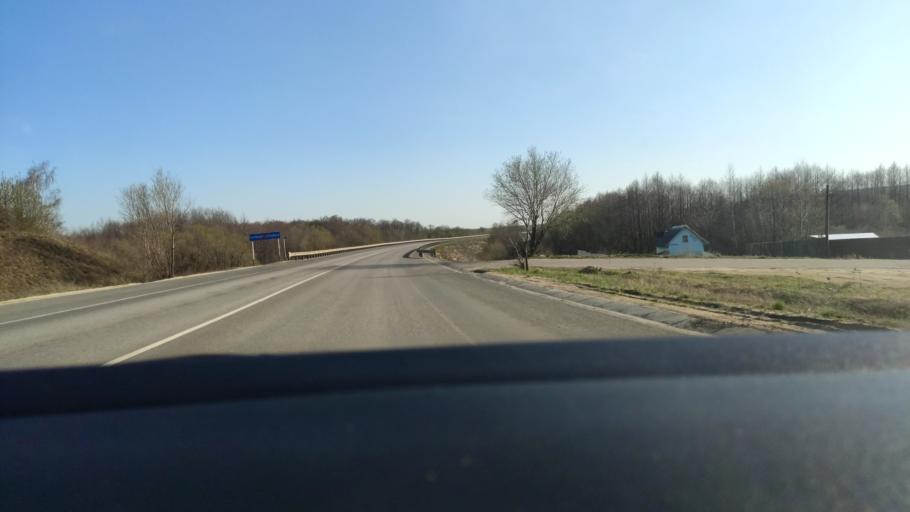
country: RU
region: Voronezj
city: Kolodeznyy
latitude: 51.3476
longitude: 39.1735
